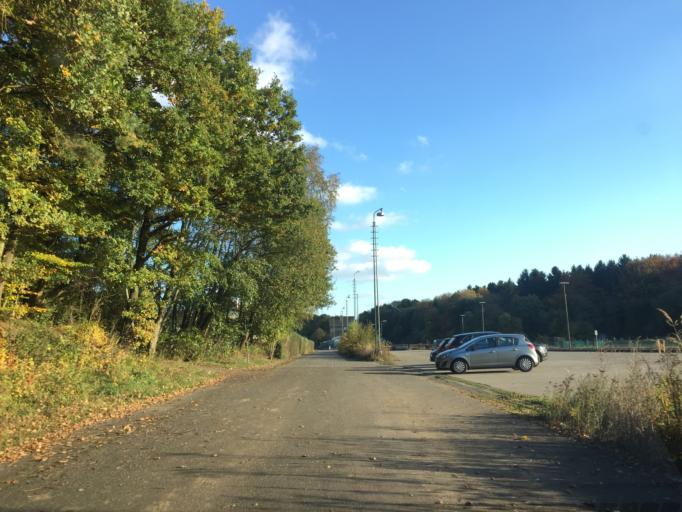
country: DE
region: Rheinland-Pfalz
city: Steinefrenz
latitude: 50.4498
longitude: 7.9363
